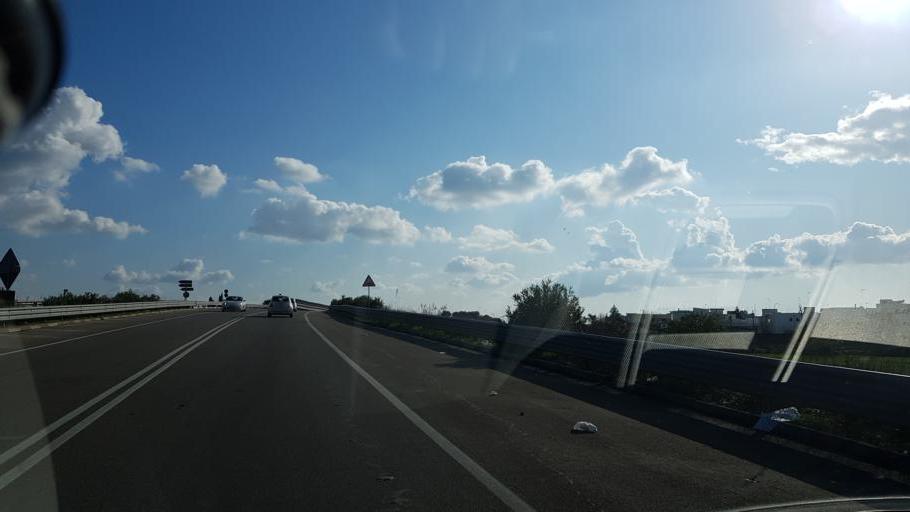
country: IT
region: Apulia
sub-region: Provincia di Lecce
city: Salice Salentino
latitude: 40.3899
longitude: 17.9687
